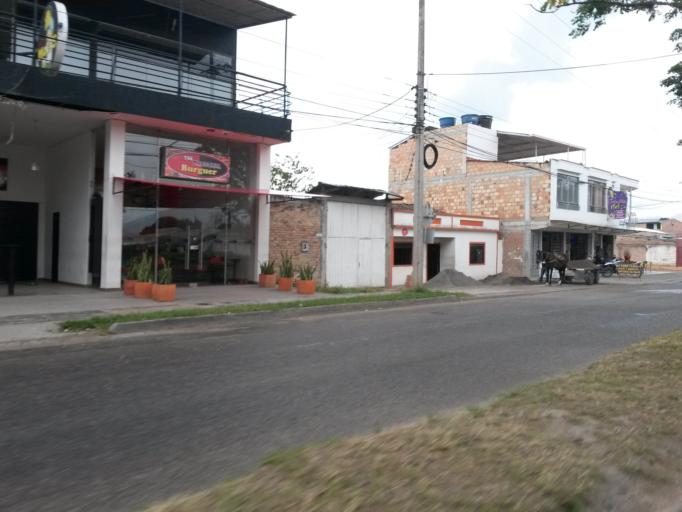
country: CO
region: Huila
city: Pitalito
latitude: 1.8466
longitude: -76.0664
